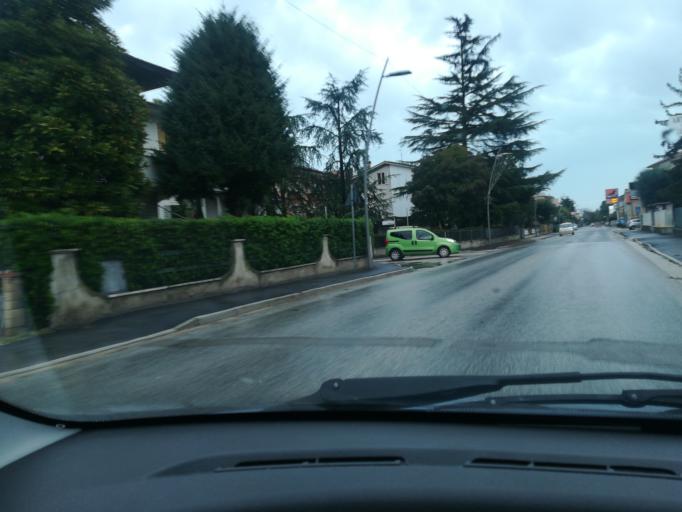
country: IT
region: The Marches
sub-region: Provincia di Macerata
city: Trodica
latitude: 43.2747
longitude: 13.5940
